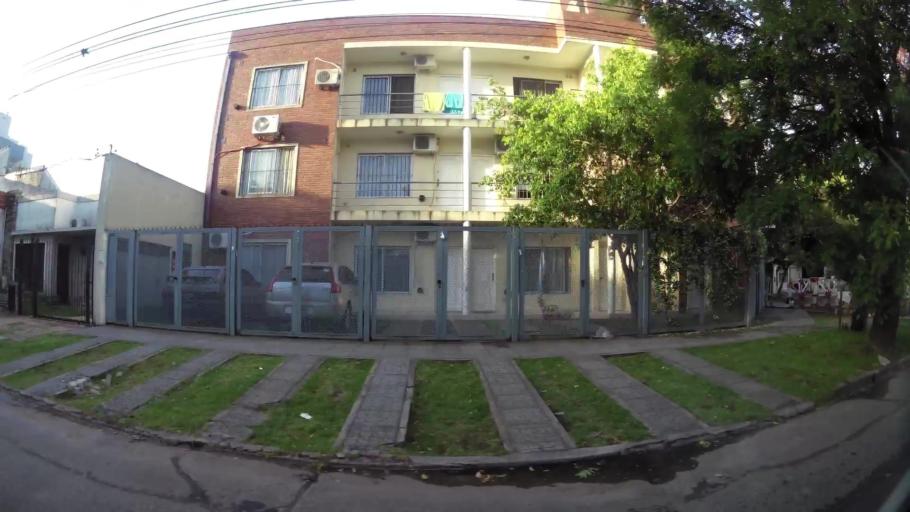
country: AR
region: Buenos Aires
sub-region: Partido de Moron
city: Moron
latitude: -34.6547
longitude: -58.6278
